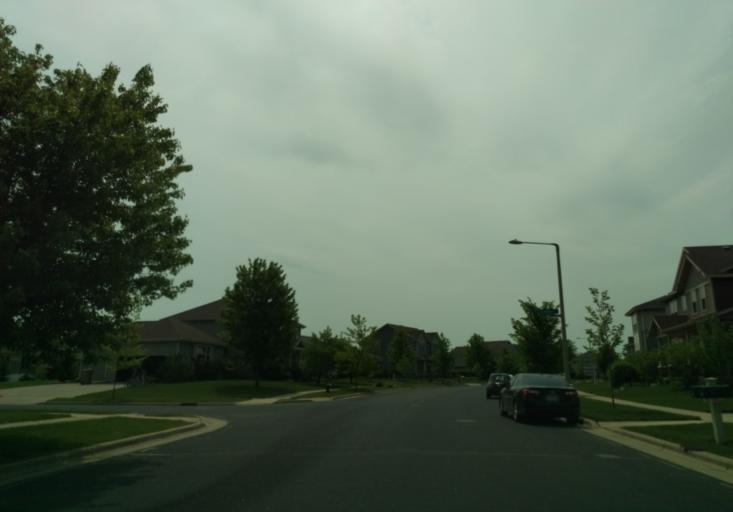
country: US
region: Wisconsin
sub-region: Dane County
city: Monona
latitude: 43.0884
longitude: -89.2743
